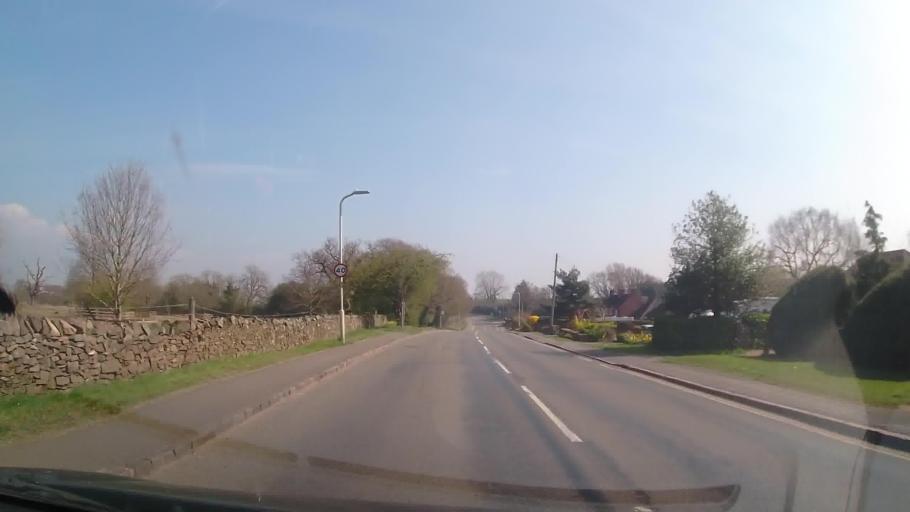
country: GB
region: England
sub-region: Leicestershire
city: Anstey
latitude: 52.6808
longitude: -1.2157
